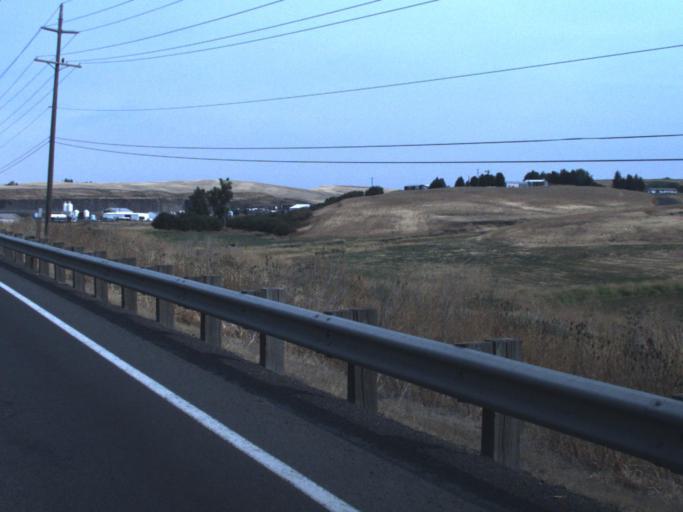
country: US
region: Washington
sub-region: Whitman County
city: Pullman
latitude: 46.7529
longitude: -117.1705
